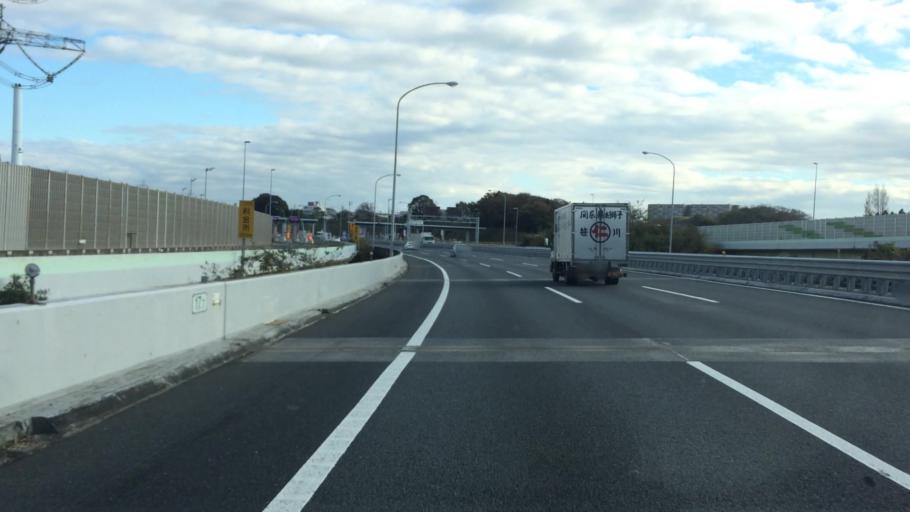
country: JP
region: Chiba
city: Yotsukaido
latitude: 35.6652
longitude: 140.1088
